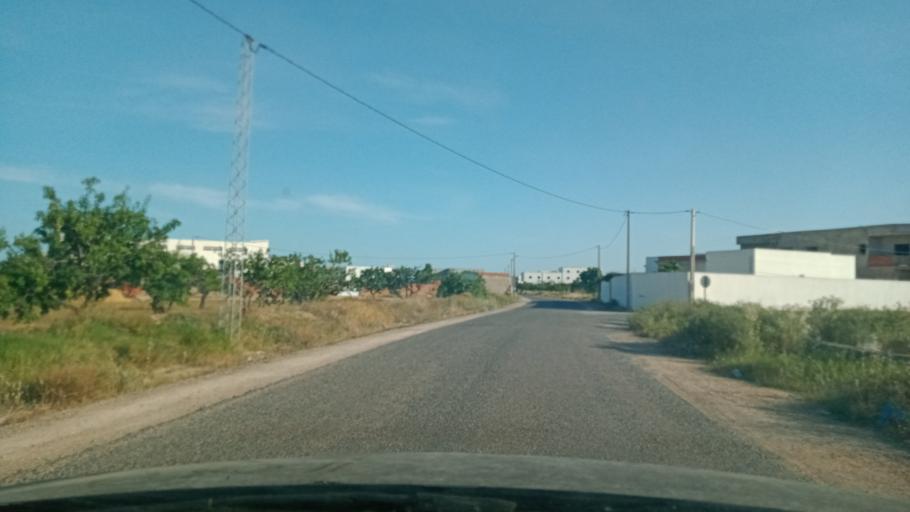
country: TN
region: Safaqis
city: Sfax
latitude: 34.8180
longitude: 10.7360
